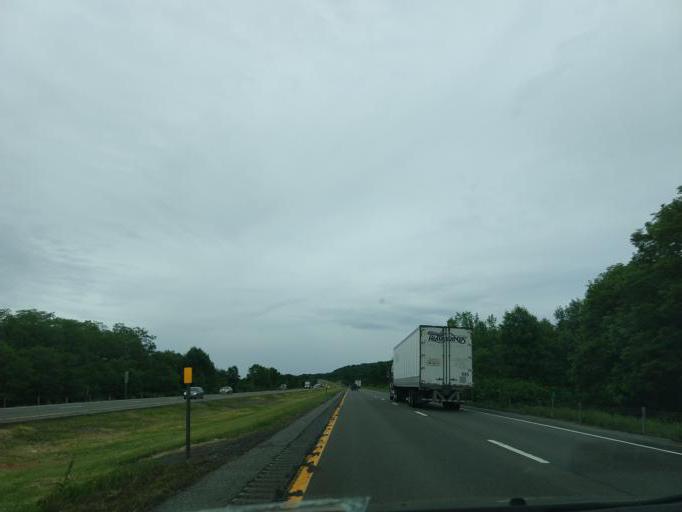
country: US
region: New York
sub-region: Chenango County
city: Lakeview
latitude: 42.3079
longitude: -75.9455
